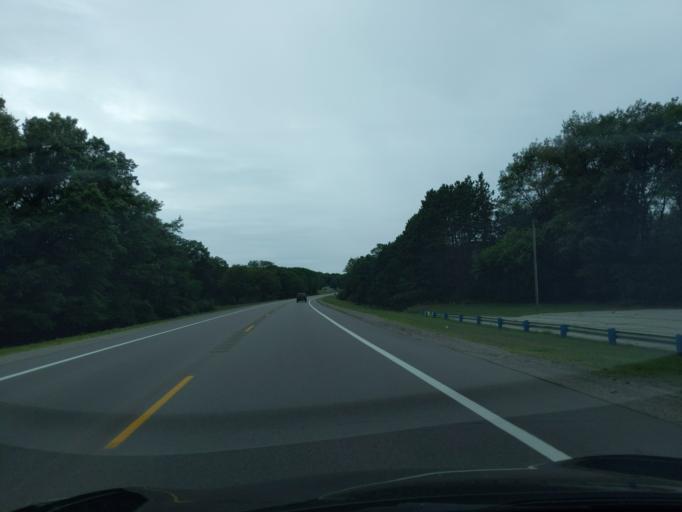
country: US
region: Michigan
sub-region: Clare County
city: Harrison
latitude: 44.0182
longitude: -84.8210
